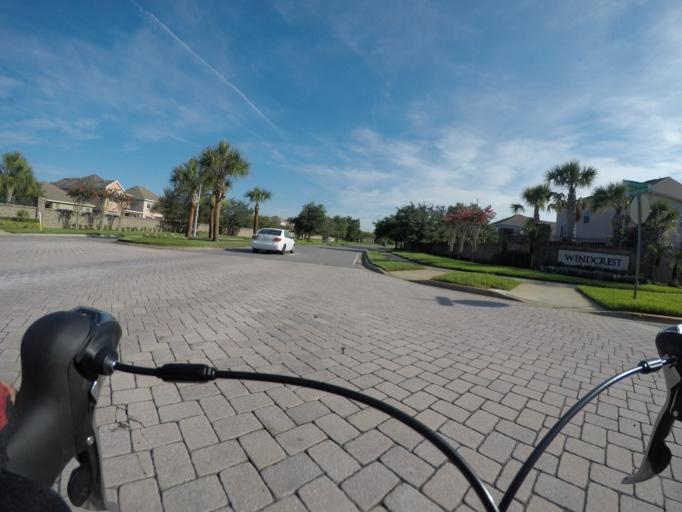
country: US
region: Florida
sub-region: Osceola County
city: Buenaventura Lakes
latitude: 28.3575
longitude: -81.3488
